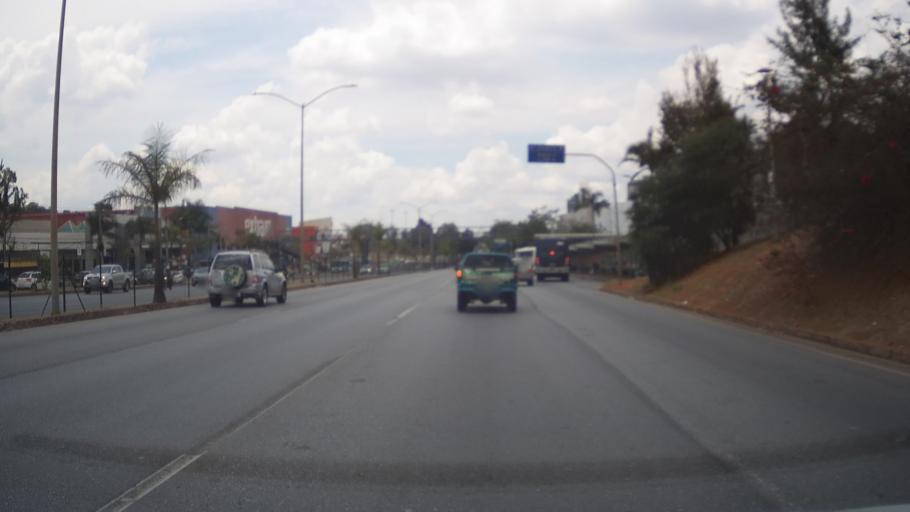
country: BR
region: Minas Gerais
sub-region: Belo Horizonte
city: Belo Horizonte
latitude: -19.9768
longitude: -43.9472
